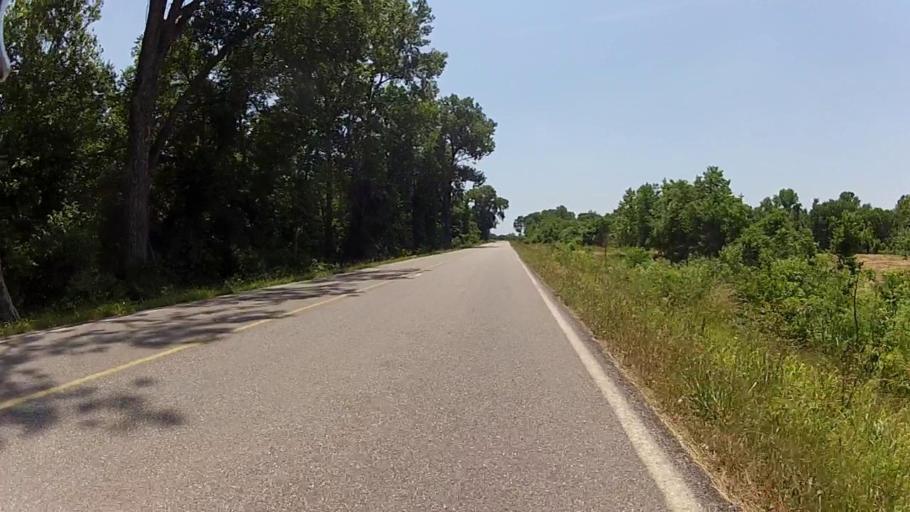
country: US
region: Kansas
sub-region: Montgomery County
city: Cherryvale
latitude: 37.2091
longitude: -95.5391
